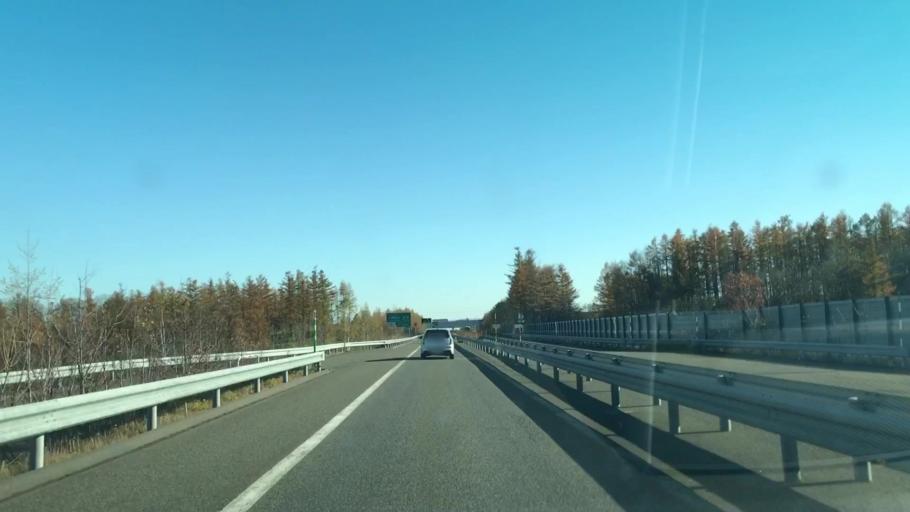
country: JP
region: Hokkaido
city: Otofuke
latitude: 43.0011
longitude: 142.8490
